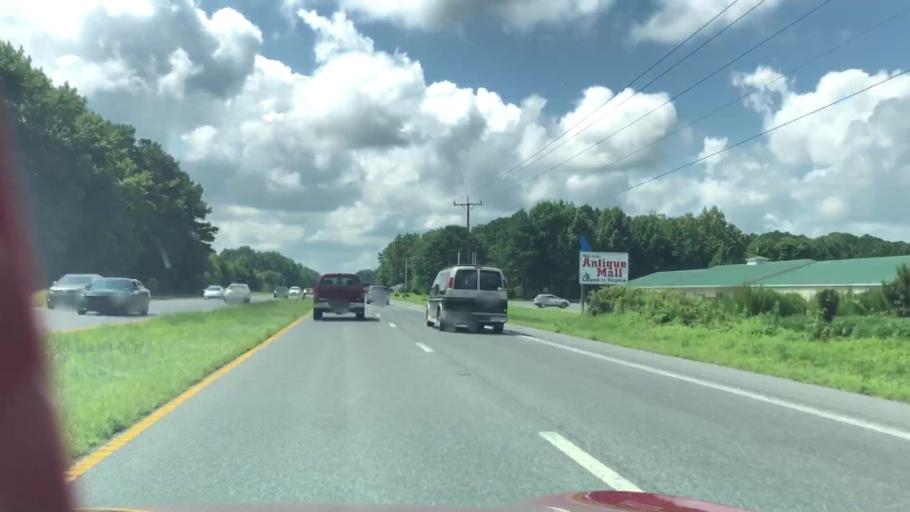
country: US
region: Virginia
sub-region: Northampton County
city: Exmore
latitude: 37.6047
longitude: -75.7726
